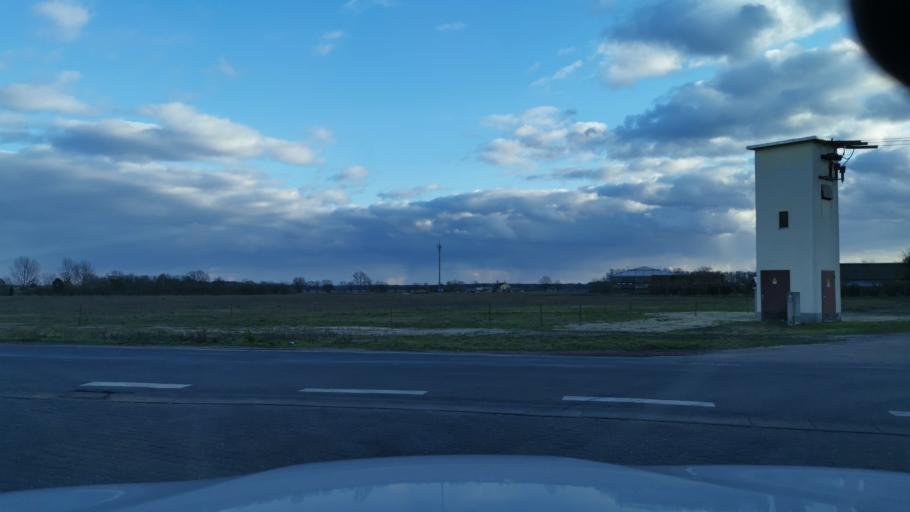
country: DE
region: Saxony-Anhalt
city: Holzdorf
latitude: 51.8133
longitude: 13.2093
